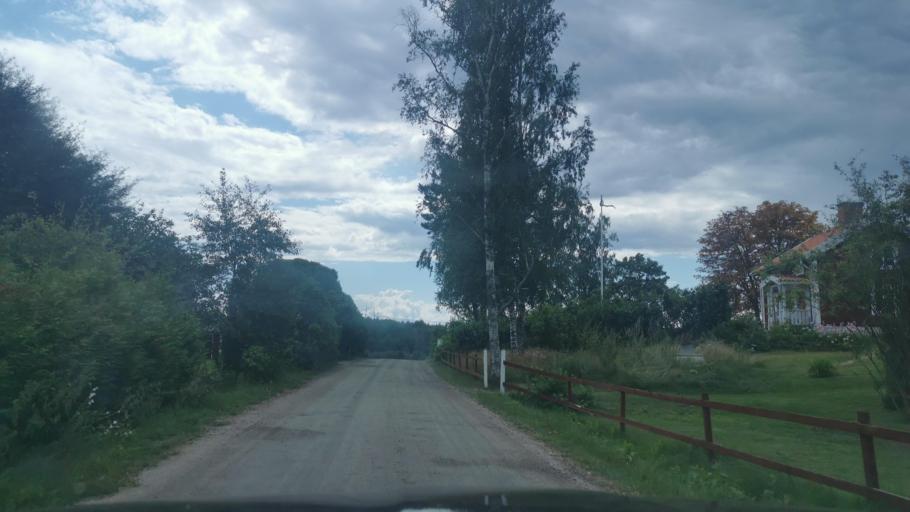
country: SE
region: OEstergoetland
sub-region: Norrkopings Kommun
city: Svartinge
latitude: 58.7202
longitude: 15.9499
